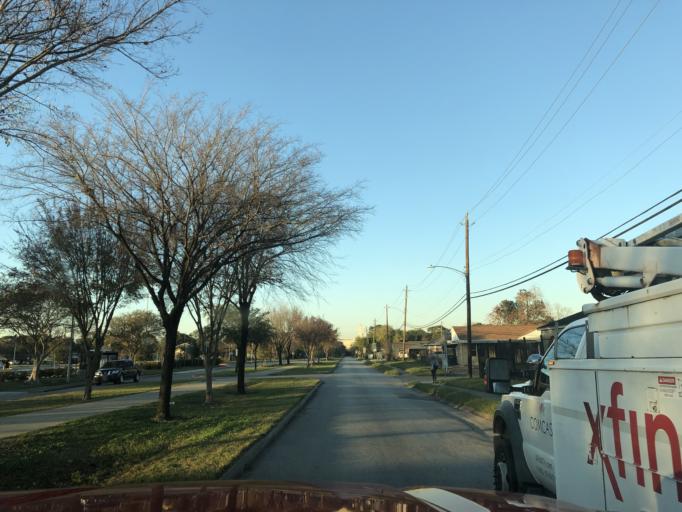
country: US
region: Texas
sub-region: Harris County
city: Jacinto City
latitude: 29.7629
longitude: -95.2699
